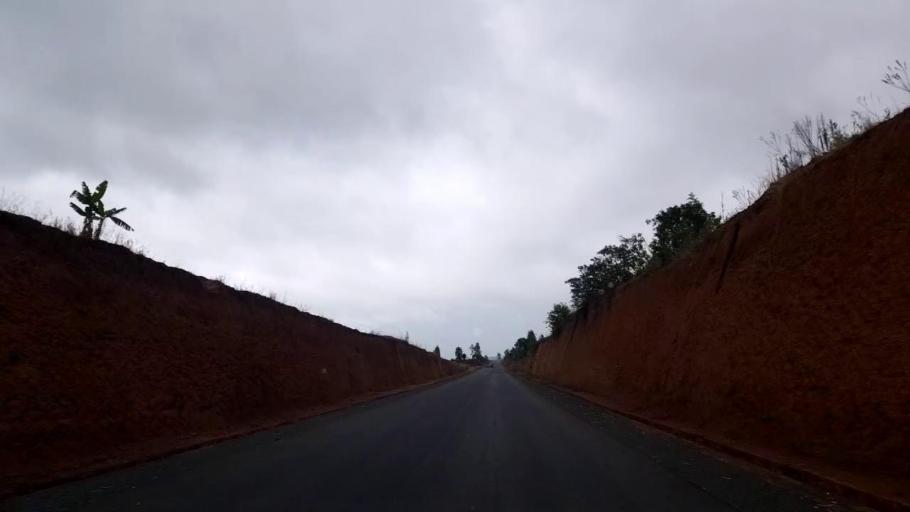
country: RW
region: Northern Province
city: Byumba
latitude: -1.4303
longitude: 30.2634
